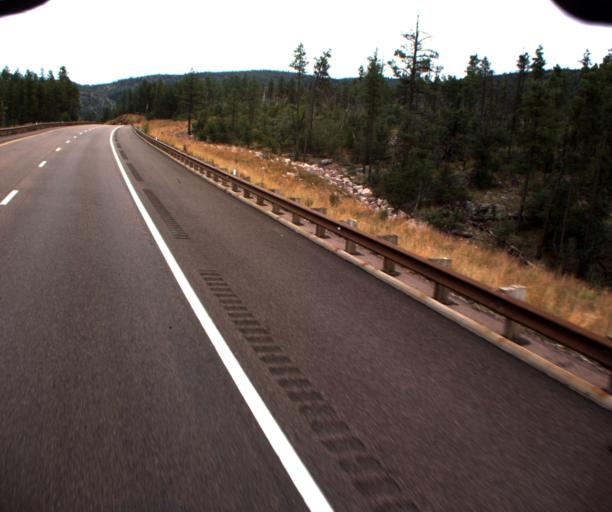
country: US
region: Arizona
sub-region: Gila County
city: Star Valley
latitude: 34.3157
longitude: -111.0591
